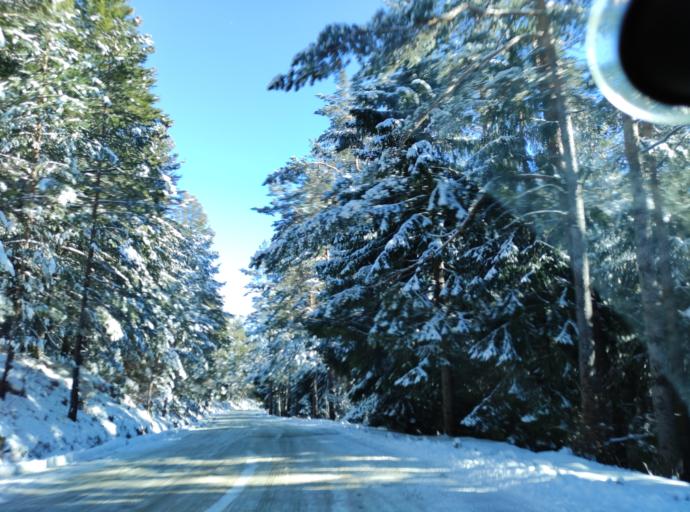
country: BG
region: Sofia-Capital
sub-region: Stolichna Obshtina
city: Sofia
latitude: 42.5887
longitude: 23.3013
